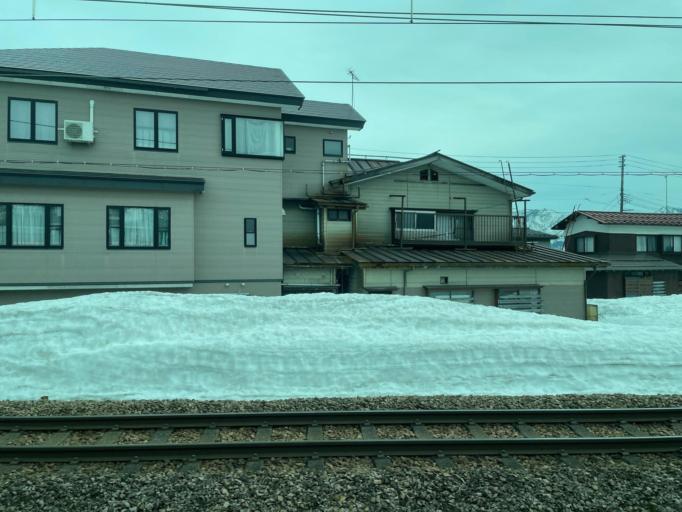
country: JP
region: Niigata
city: Shiozawa
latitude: 37.0425
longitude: 138.8511
